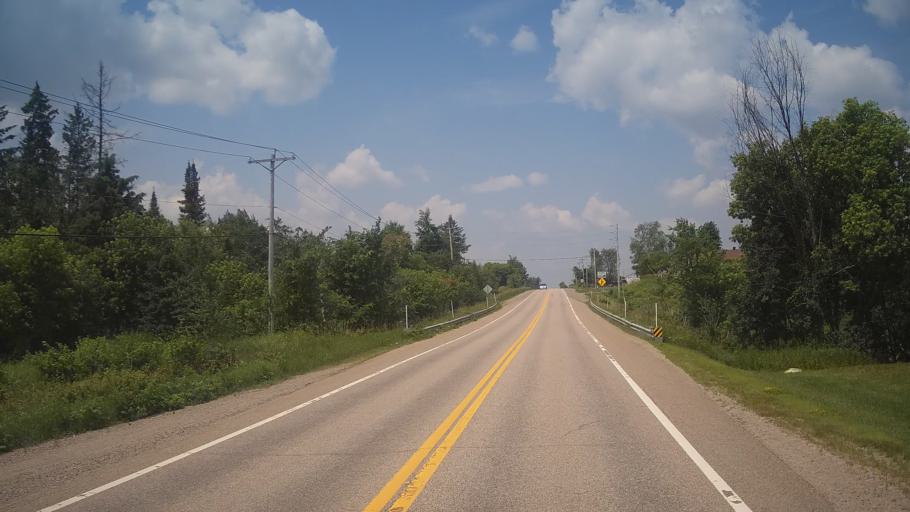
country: CA
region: Quebec
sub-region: Outaouais
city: Shawville
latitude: 45.5862
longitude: -76.4577
